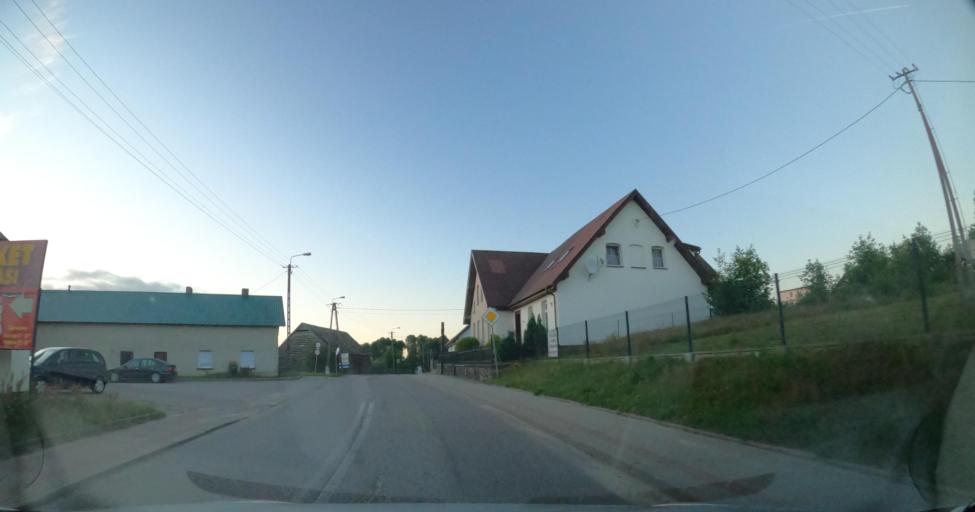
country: PL
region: Pomeranian Voivodeship
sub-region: Powiat wejherowski
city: Linia
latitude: 54.4518
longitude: 17.9358
